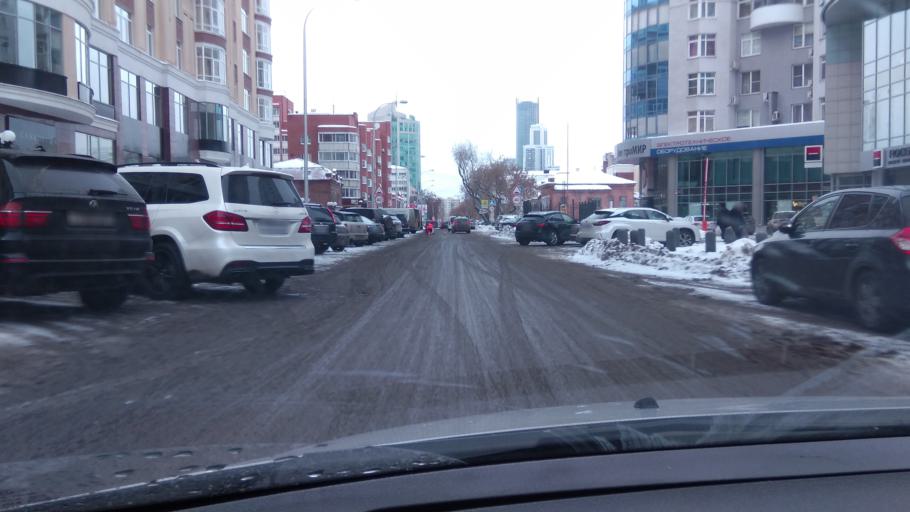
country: RU
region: Sverdlovsk
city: Yekaterinburg
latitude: 56.8305
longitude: 60.5935
